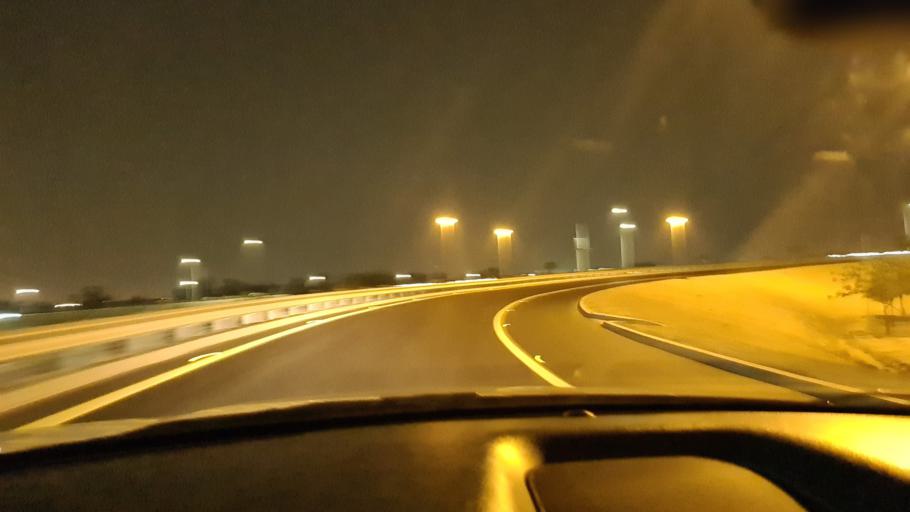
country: SA
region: Eastern Province
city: Al Jubayl
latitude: 27.1365
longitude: 49.5596
